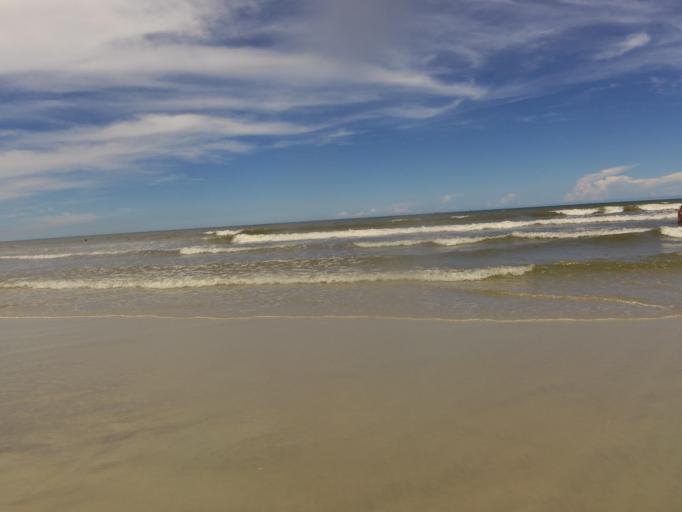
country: US
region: Florida
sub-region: Saint Johns County
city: Saint Augustine Beach
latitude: 29.8282
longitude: -81.2626
